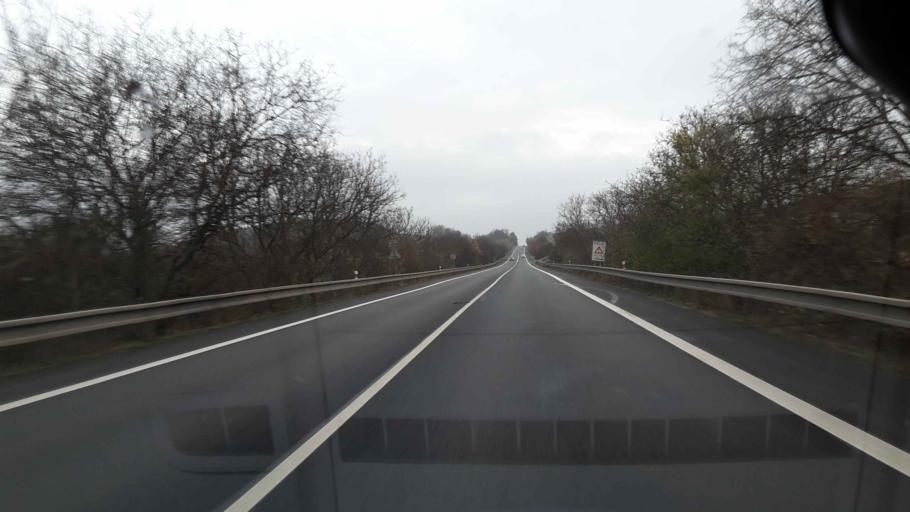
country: CZ
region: South Moravian
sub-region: Okres Brno-Venkov
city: Lelekovice
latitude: 49.2907
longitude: 16.5608
